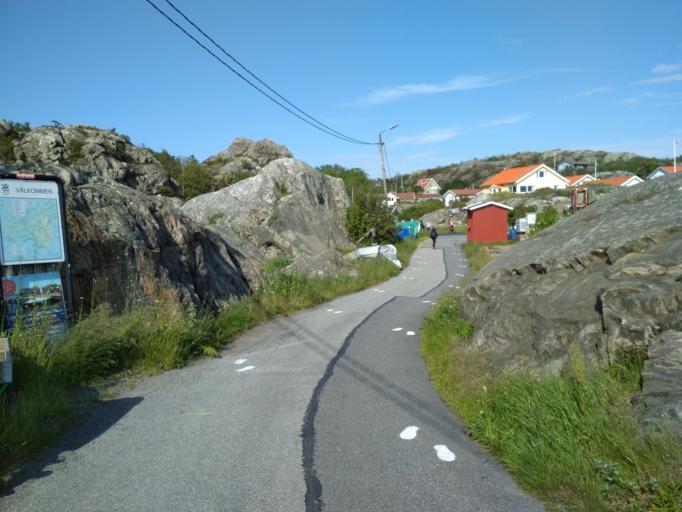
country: SE
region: Vaestra Goetaland
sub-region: Goteborg
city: Styrso
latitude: 57.6357
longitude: 11.7673
